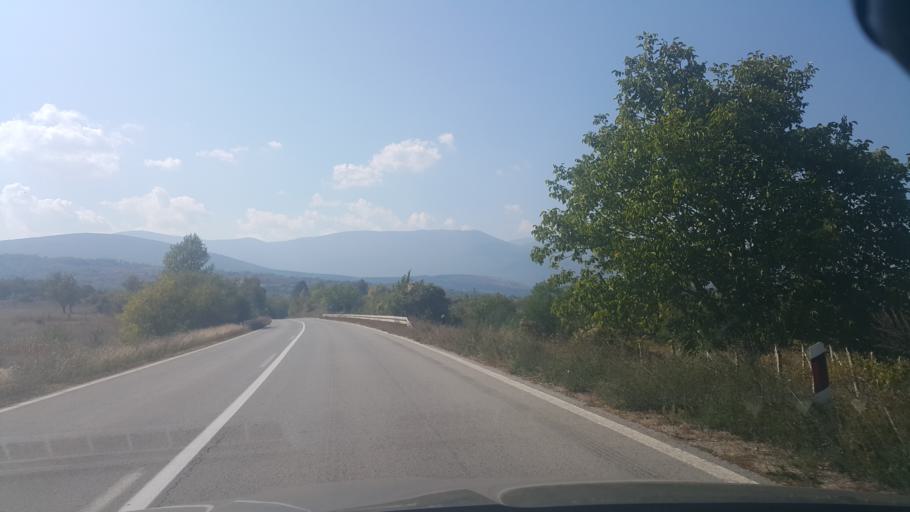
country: RS
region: Central Serbia
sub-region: Pirotski Okrug
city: Bela Palanka
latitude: 43.2259
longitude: 22.3700
